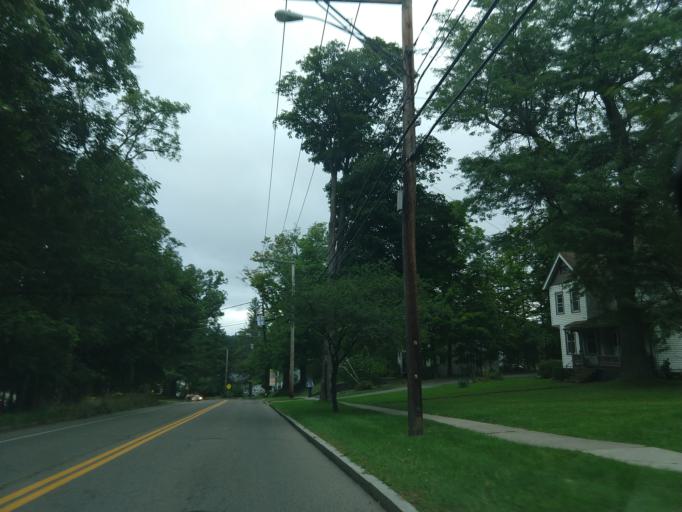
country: US
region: New York
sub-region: Tompkins County
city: South Hill
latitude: 42.4321
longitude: -76.4919
